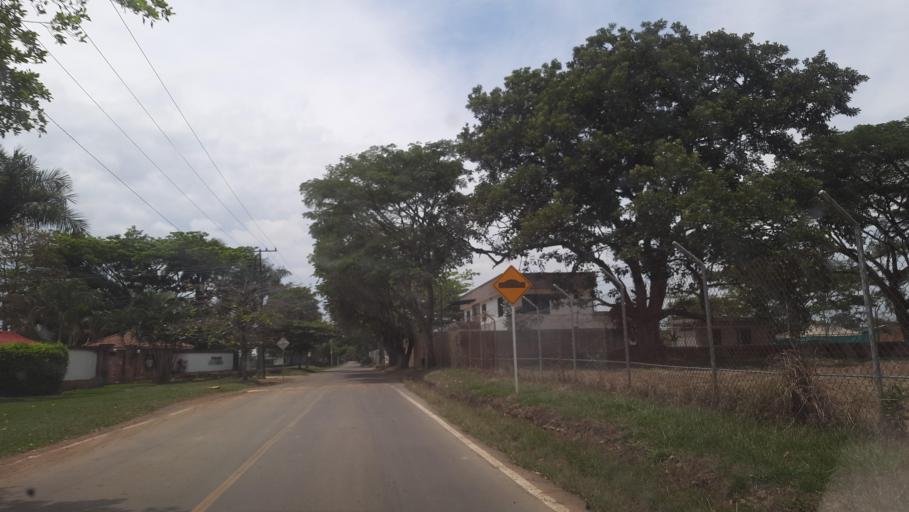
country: CO
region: Valle del Cauca
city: Jamundi
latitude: 3.2684
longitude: -76.5144
